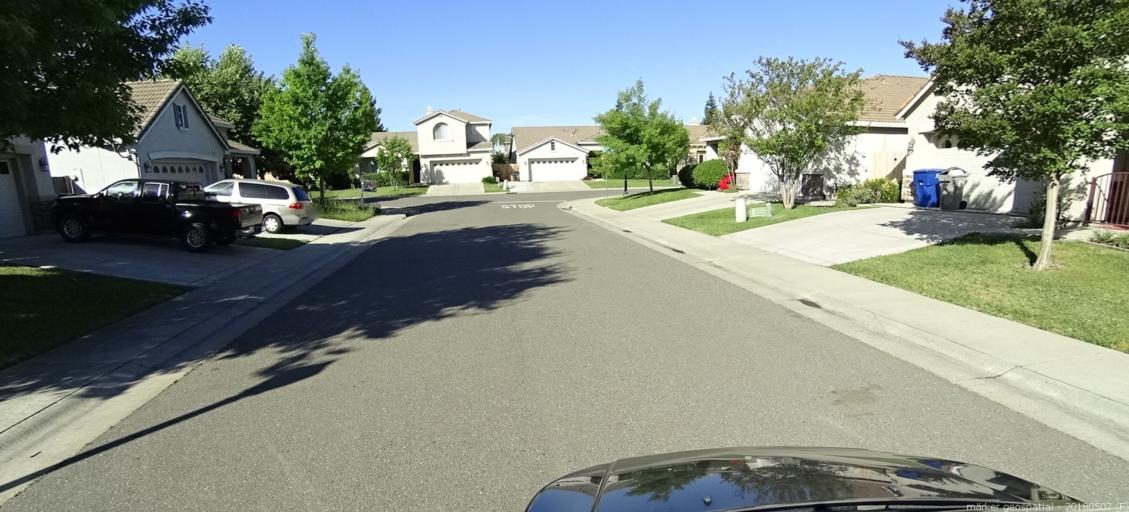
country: US
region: California
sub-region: Sacramento County
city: Rio Linda
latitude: 38.6753
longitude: -121.4980
